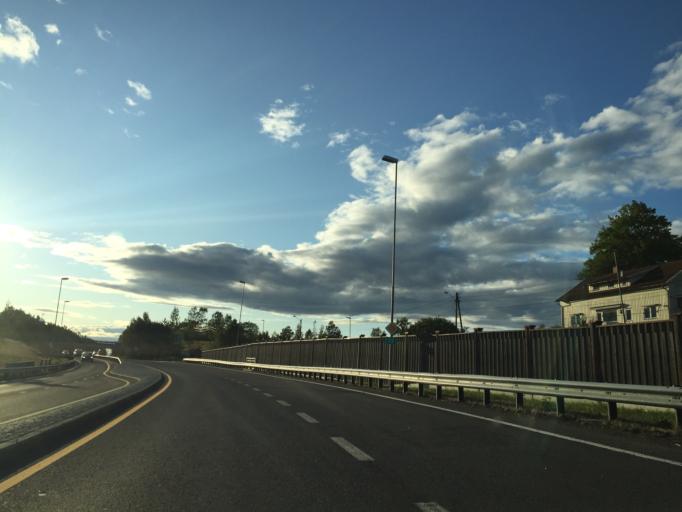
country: NO
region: Akershus
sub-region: Fet
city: Fetsund
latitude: 59.9302
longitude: 11.1473
